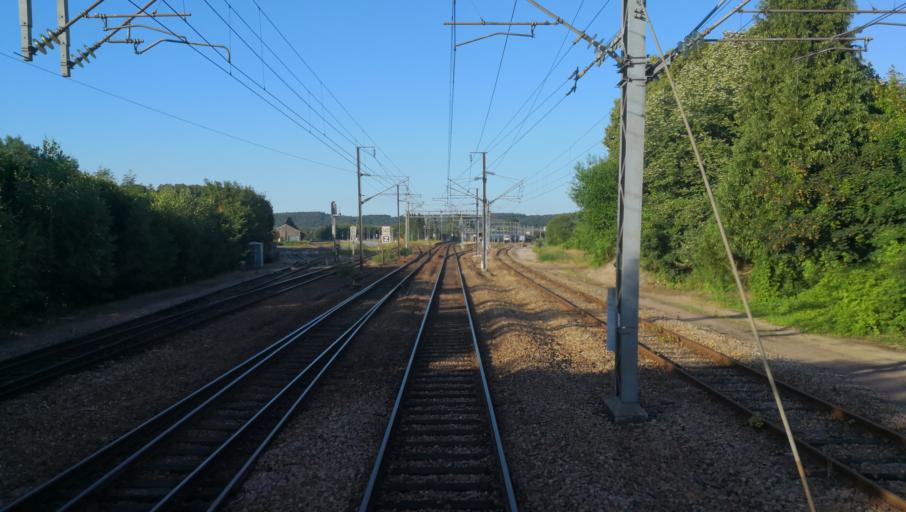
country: FR
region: Haute-Normandie
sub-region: Departement de l'Eure
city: Serquigny
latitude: 49.1055
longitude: 0.7152
